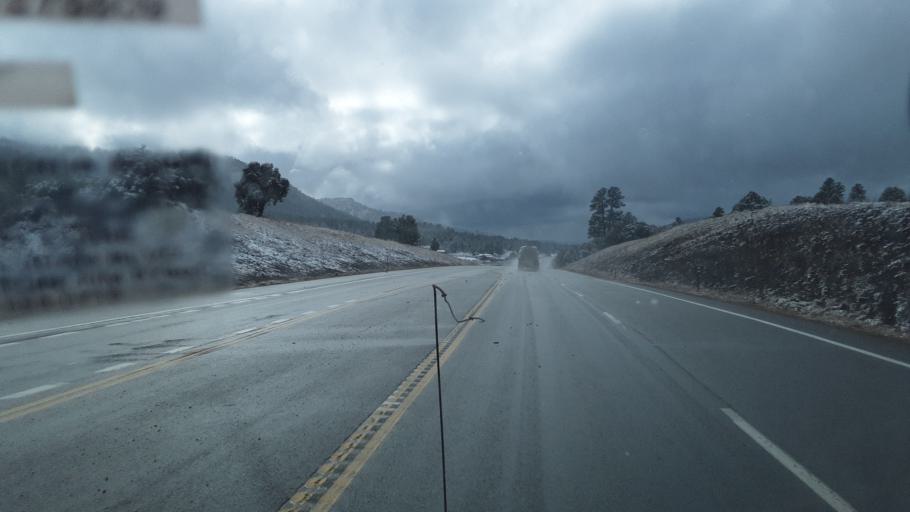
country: US
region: Colorado
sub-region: Archuleta County
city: Pagosa Springs
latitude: 37.2319
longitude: -107.1857
